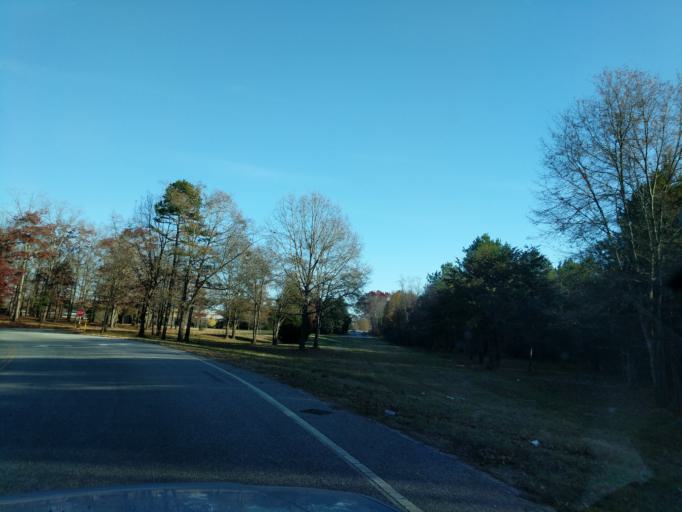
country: US
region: South Carolina
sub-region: Spartanburg County
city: Wellford
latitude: 34.9364
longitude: -82.0695
